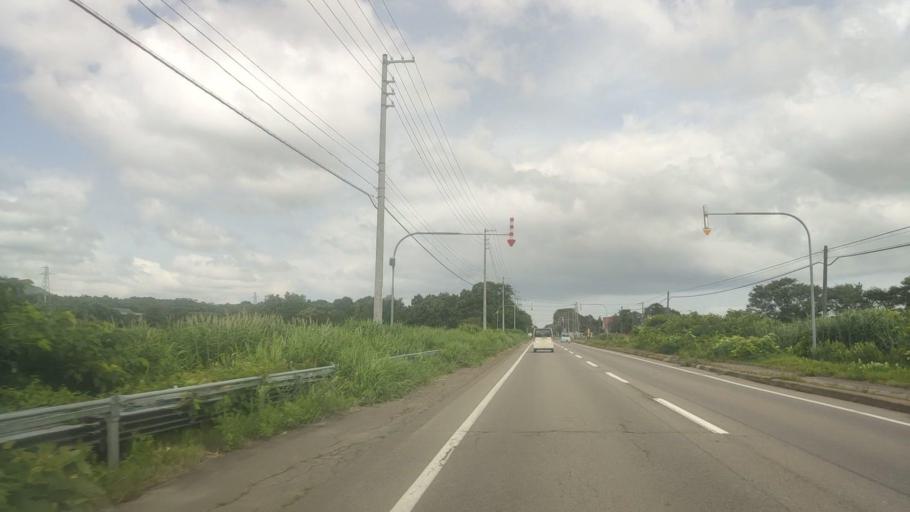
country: JP
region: Hokkaido
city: Nanae
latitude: 42.0329
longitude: 140.6088
